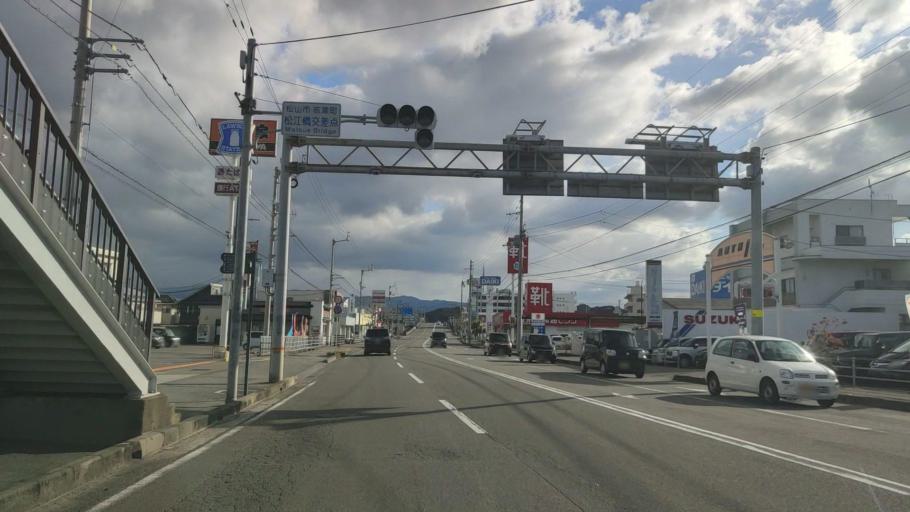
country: JP
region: Ehime
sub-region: Shikoku-chuo Shi
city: Matsuyama
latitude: 33.8575
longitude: 132.7192
